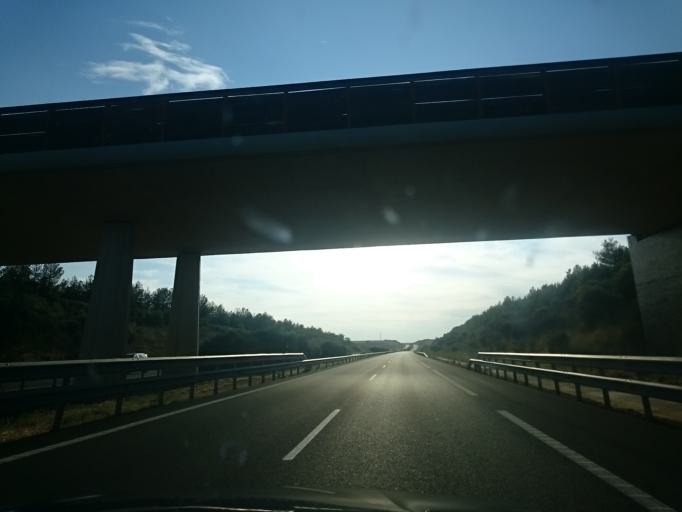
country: ES
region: Castille and Leon
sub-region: Provincia de Palencia
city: Ledigos
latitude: 42.3613
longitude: -4.8431
